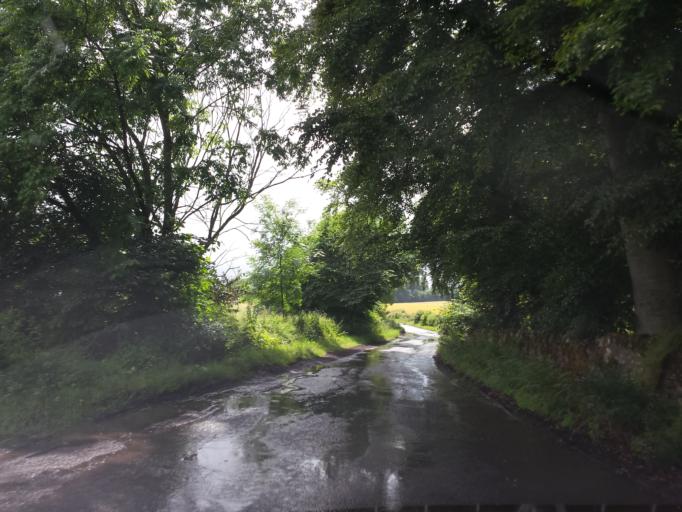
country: GB
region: Scotland
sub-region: The Scottish Borders
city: Saint Boswells
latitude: 55.5916
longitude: -2.6440
